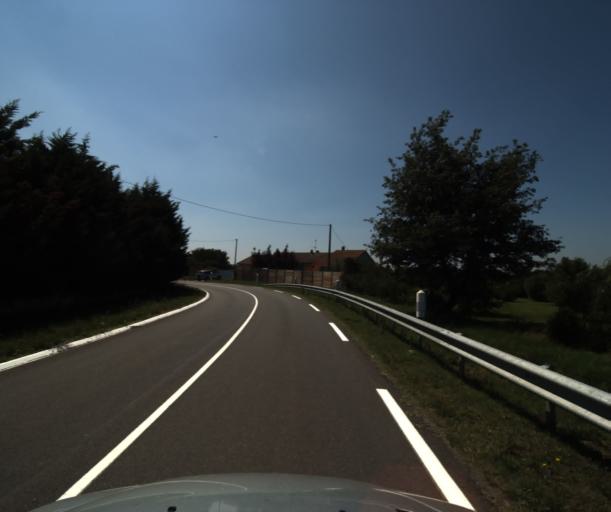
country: FR
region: Midi-Pyrenees
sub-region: Departement de la Haute-Garonne
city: Labastidette
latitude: 43.4374
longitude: 1.2530
